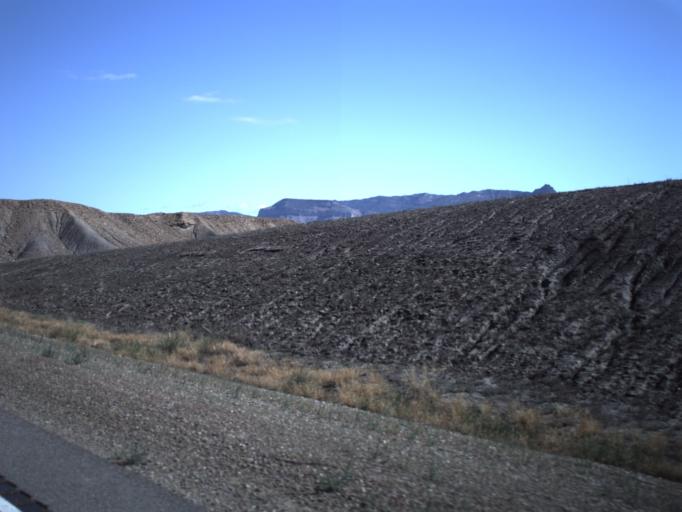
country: US
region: Utah
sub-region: Carbon County
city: East Carbon City
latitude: 39.3431
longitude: -110.3740
